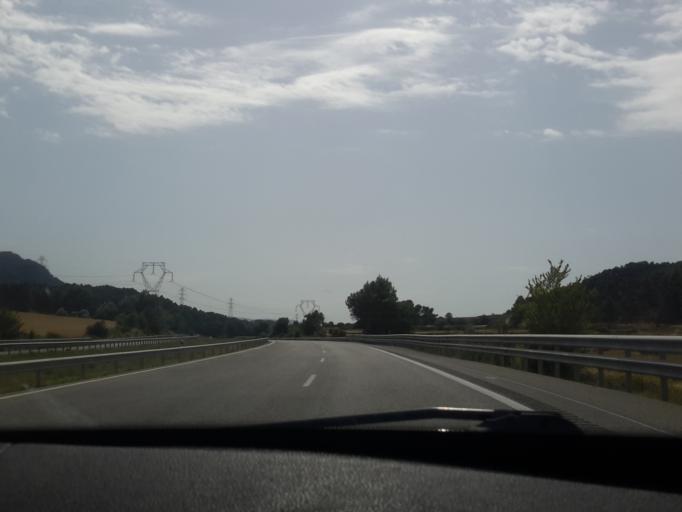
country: ES
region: Catalonia
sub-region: Provincia de Tarragona
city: Cabra del Camp
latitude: 41.3940
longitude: 1.2680
